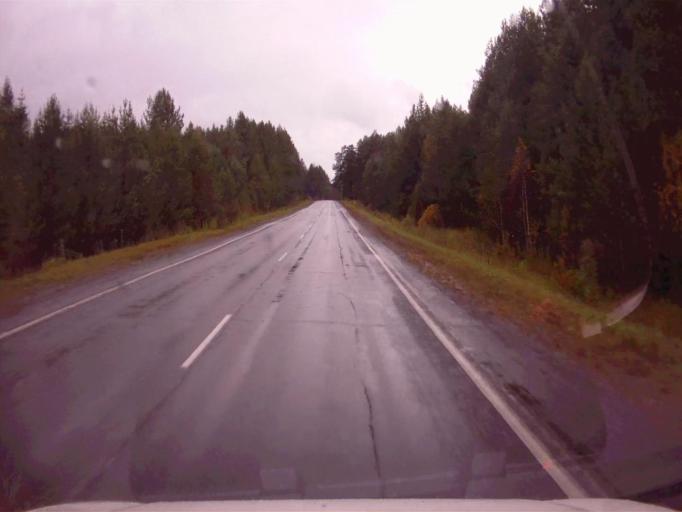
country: RU
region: Chelyabinsk
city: Verkhniy Ufaley
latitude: 56.0197
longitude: 60.3041
